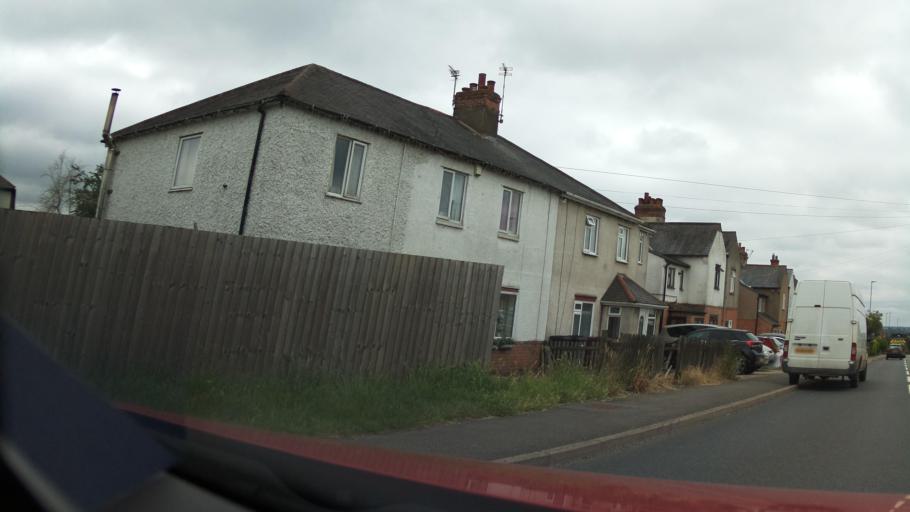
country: GB
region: England
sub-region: Leicestershire
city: Asfordby
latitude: 52.7657
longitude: -0.9275
